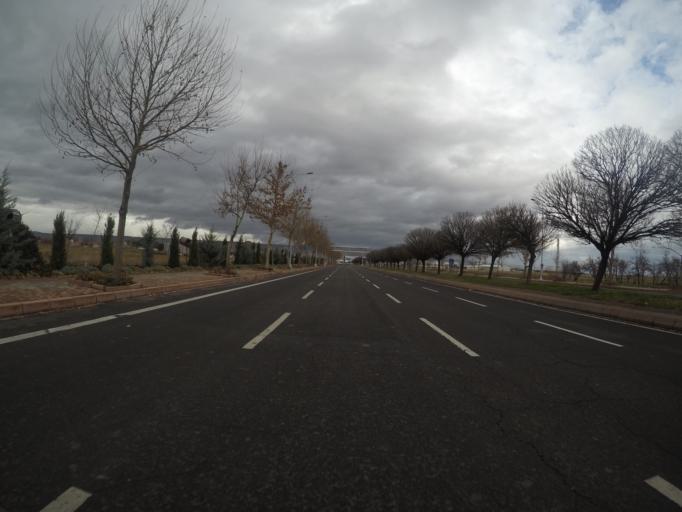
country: TR
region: Kayseri
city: Kayseri
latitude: 38.7605
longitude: 35.4821
